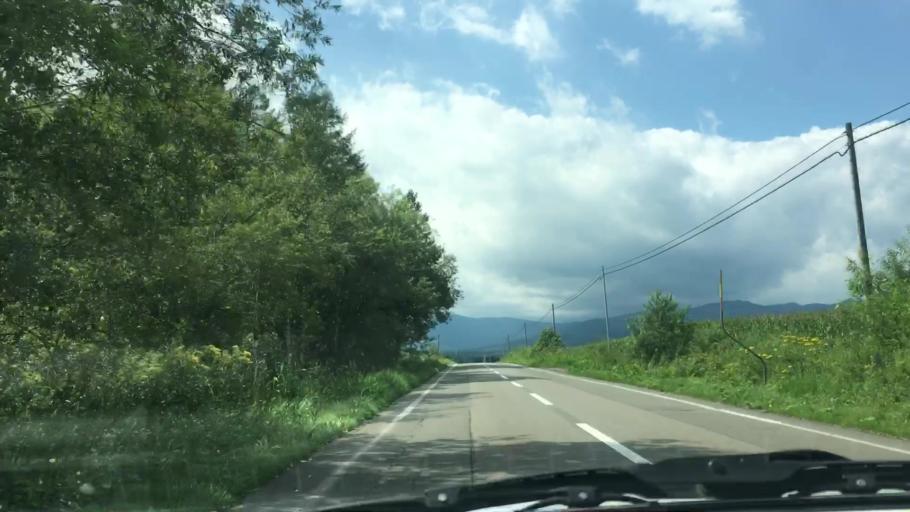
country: JP
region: Hokkaido
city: Otofuke
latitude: 43.2795
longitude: 143.3458
